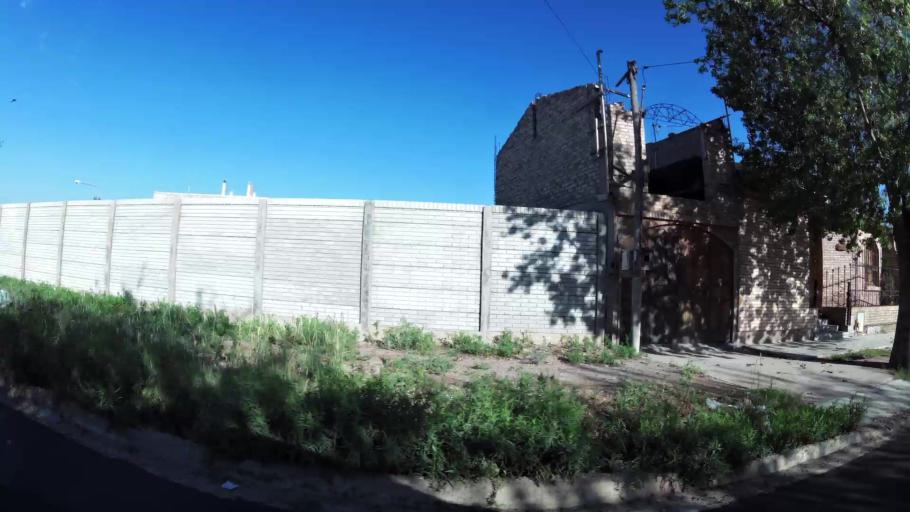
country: AR
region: Mendoza
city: Las Heras
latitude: -32.8558
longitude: -68.8176
